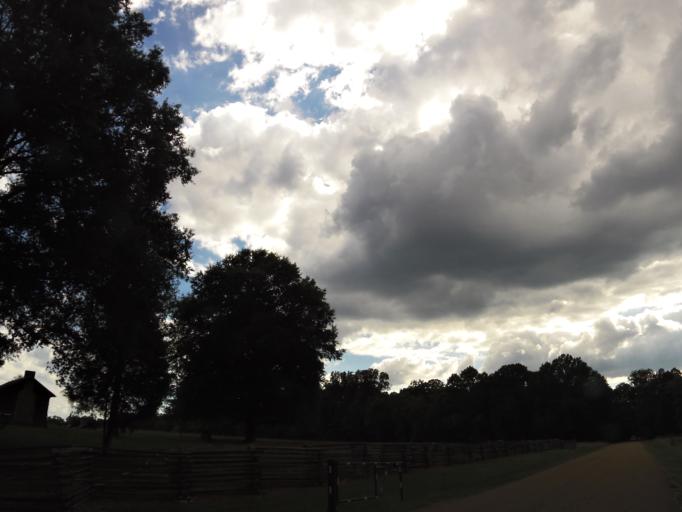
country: US
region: Georgia
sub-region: Catoosa County
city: Fort Oglethorpe
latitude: 34.9182
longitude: -85.2607
